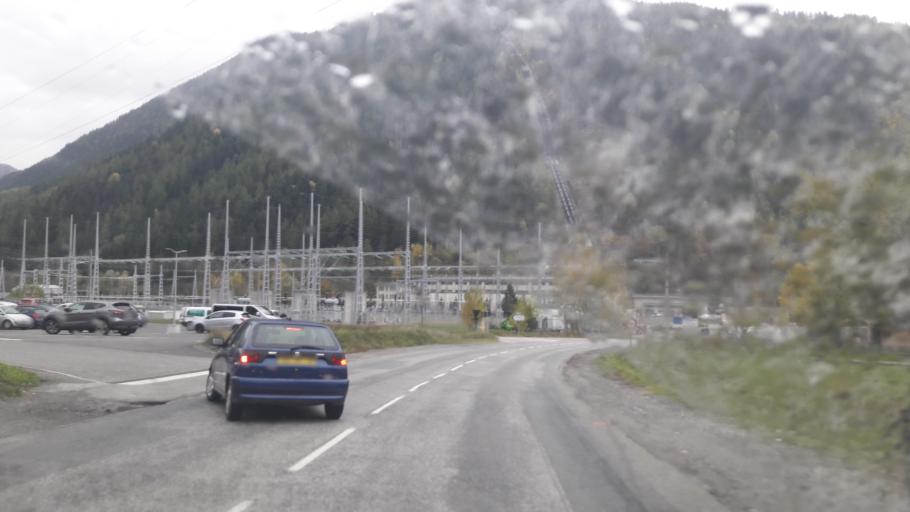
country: FR
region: Rhone-Alpes
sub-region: Departement de la Savoie
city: Seez
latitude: 45.6211
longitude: 6.7886
